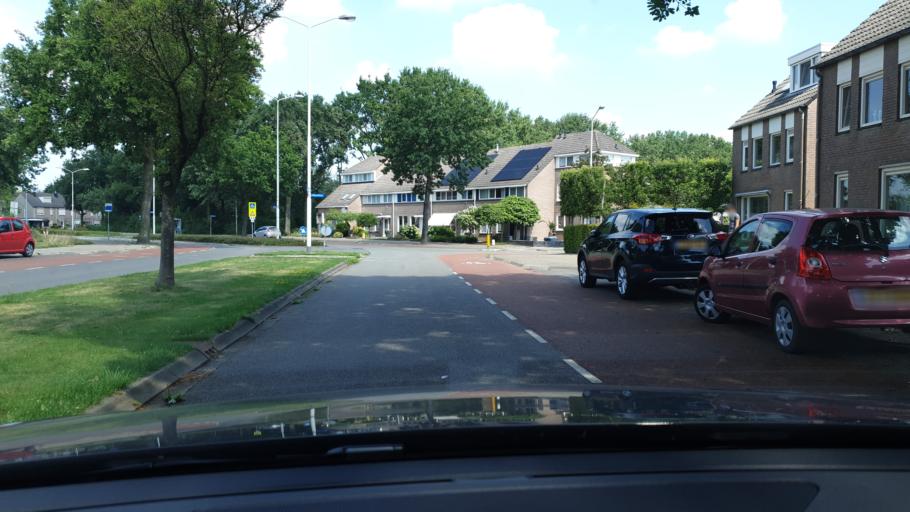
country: NL
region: North Brabant
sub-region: Gemeente Son en Breugel
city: Son
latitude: 51.4902
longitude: 5.4483
